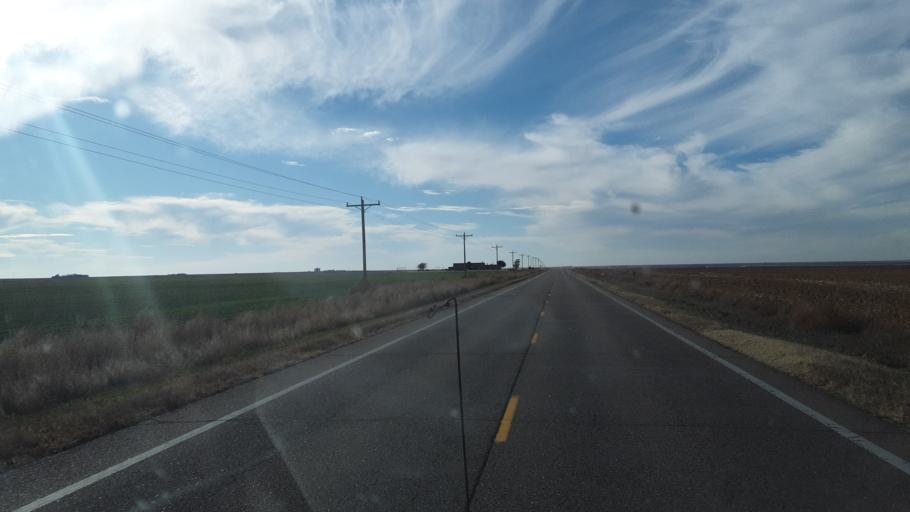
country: US
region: Kansas
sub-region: Gray County
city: Cimarron
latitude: 38.0590
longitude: -100.4939
